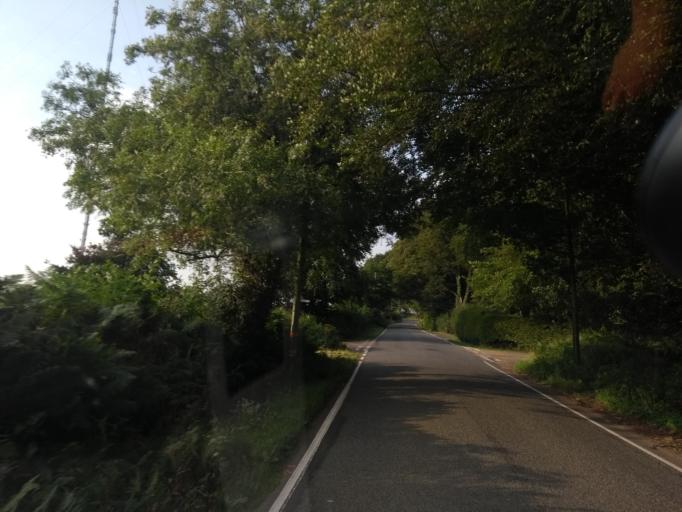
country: GB
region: England
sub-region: Devon
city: Colyton
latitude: 50.8100
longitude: -3.1074
